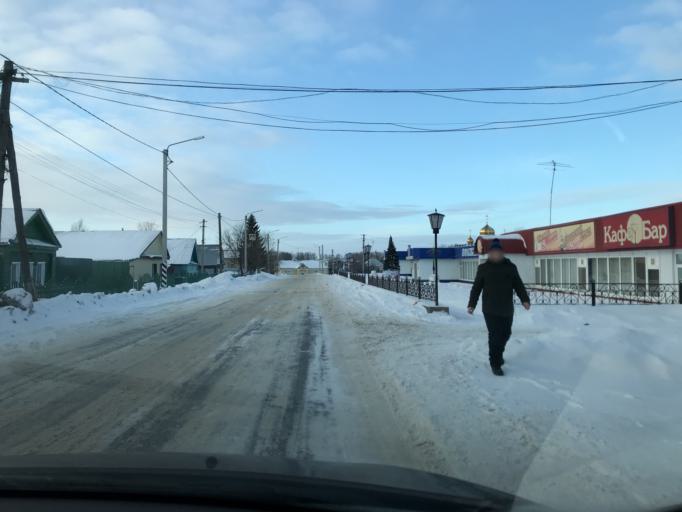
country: RU
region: Ulyanovsk
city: Undory
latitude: 54.6078
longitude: 48.3962
